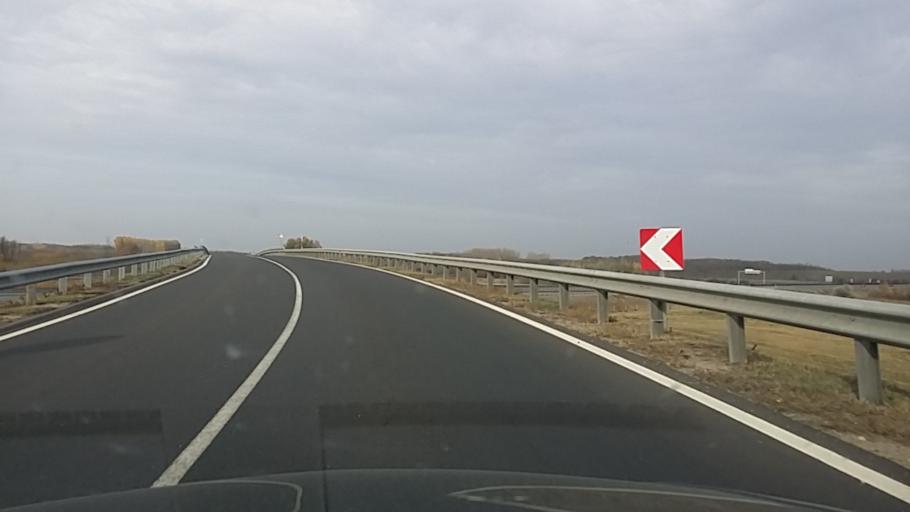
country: HU
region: Szabolcs-Szatmar-Bereg
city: Nagykallo
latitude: 47.8964
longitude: 21.8174
